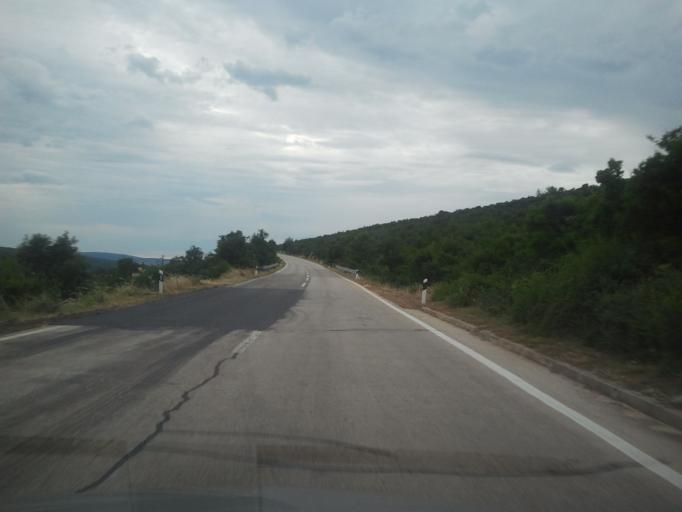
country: HR
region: Zadarska
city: Krusevo
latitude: 44.1500
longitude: 15.6326
